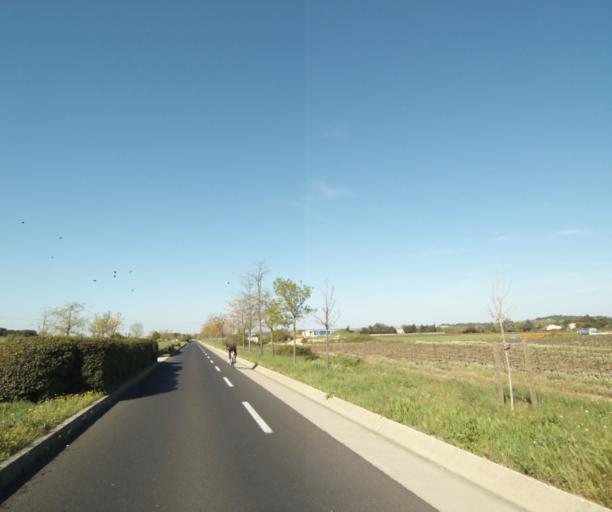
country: FR
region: Languedoc-Roussillon
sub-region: Departement de l'Herault
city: Le Cres
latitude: 43.6278
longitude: 3.9275
